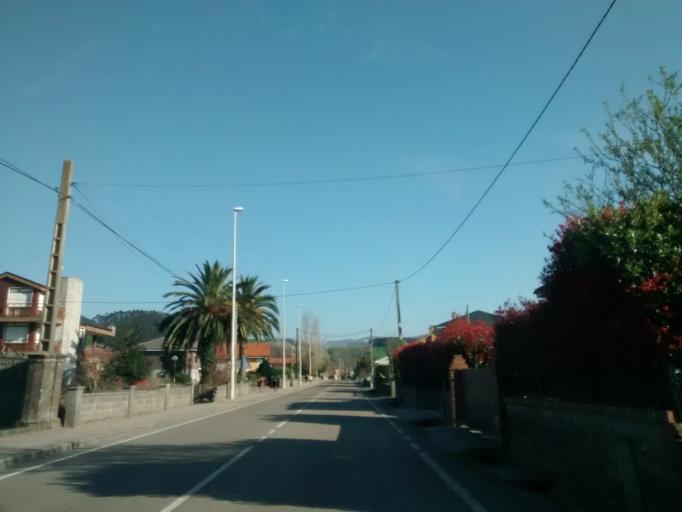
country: ES
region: Cantabria
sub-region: Provincia de Cantabria
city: Entrambasaguas
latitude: 43.3753
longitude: -3.7193
